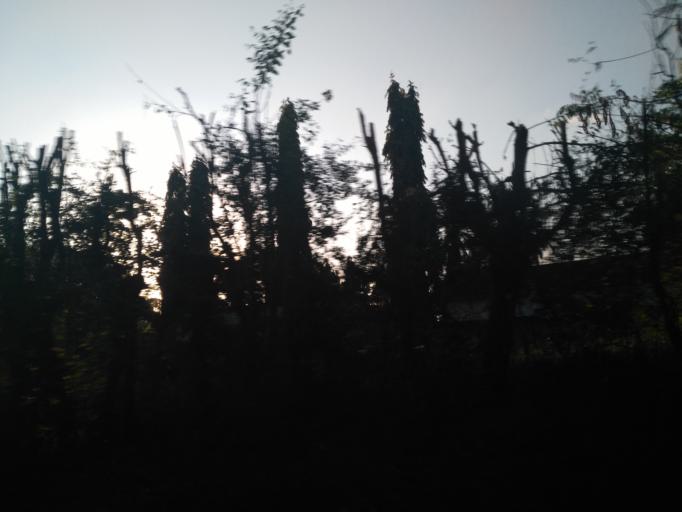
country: TZ
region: Dar es Salaam
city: Magomeni
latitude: -6.7657
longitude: 39.2498
